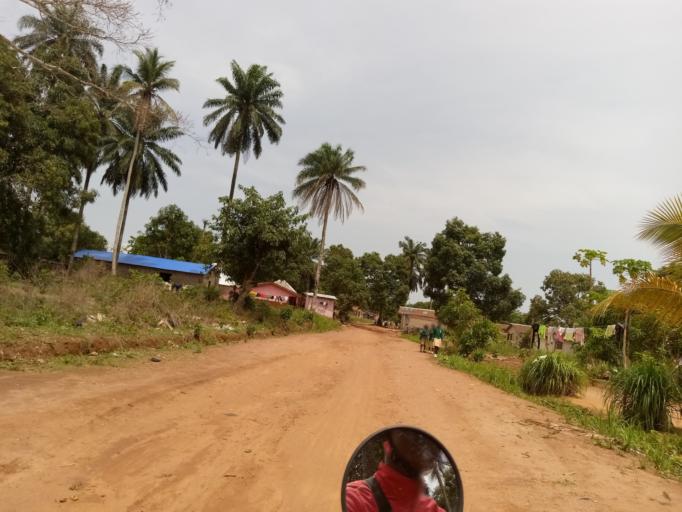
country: SL
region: Western Area
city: Waterloo
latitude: 8.3288
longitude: -13.0150
